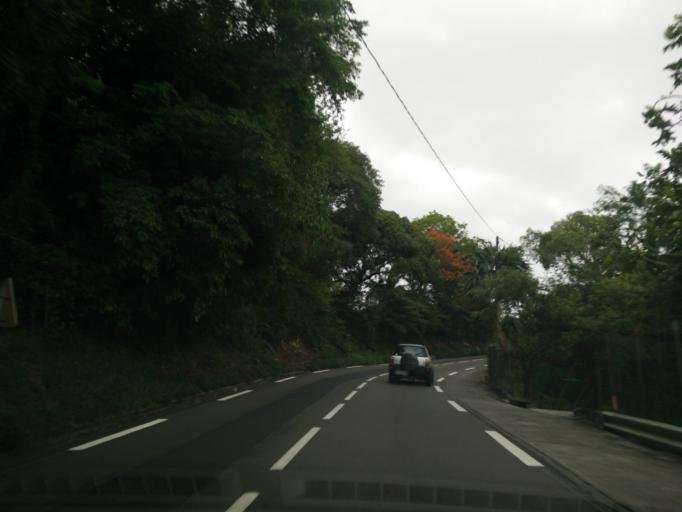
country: MQ
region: Martinique
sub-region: Martinique
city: Le Marin
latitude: 14.4819
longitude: -60.8615
